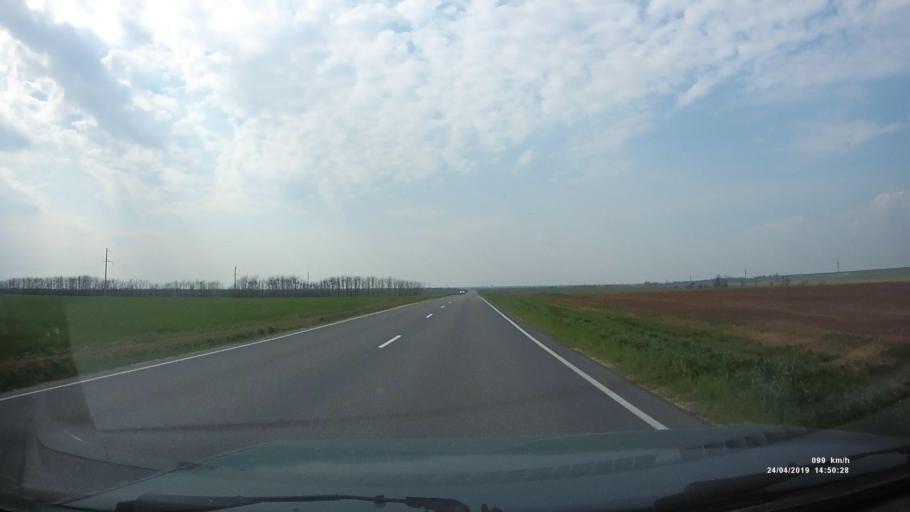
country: RU
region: Rostov
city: Remontnoye
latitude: 46.5176
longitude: 43.7189
